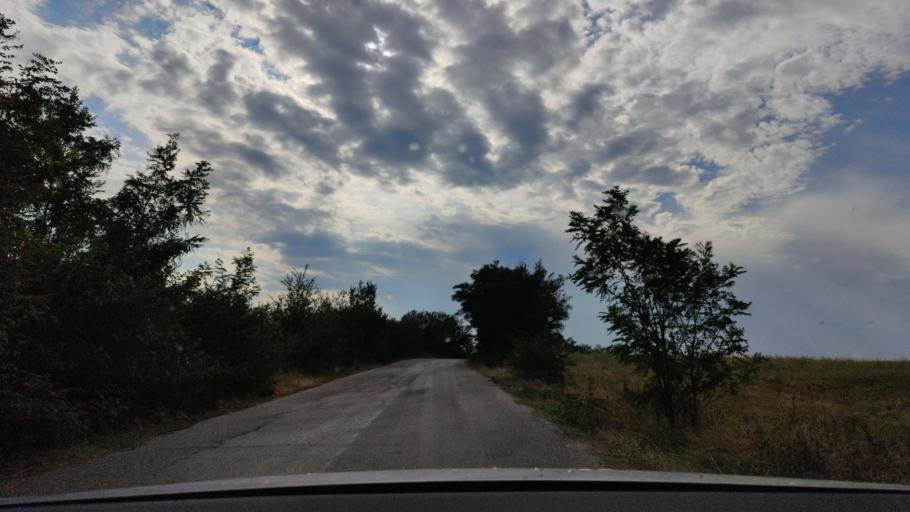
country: GR
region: Central Macedonia
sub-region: Nomos Serron
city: Kala Dendra
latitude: 41.1241
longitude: 23.4524
